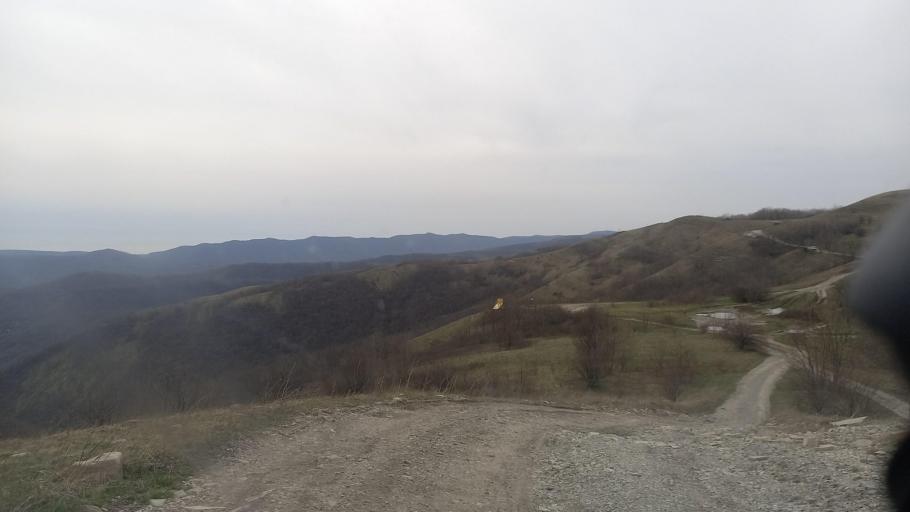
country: RU
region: Krasnodarskiy
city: Divnomorskoye
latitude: 44.6090
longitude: 38.2452
